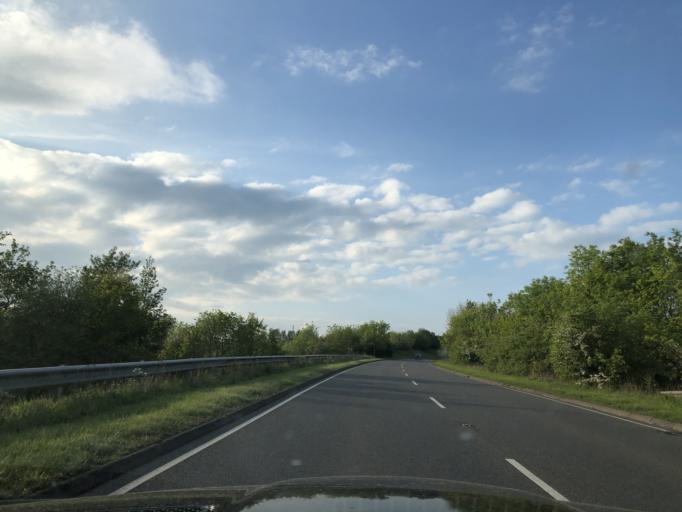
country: GB
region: England
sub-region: Warwickshire
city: Wellesbourne Mountford
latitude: 52.1364
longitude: -1.6149
